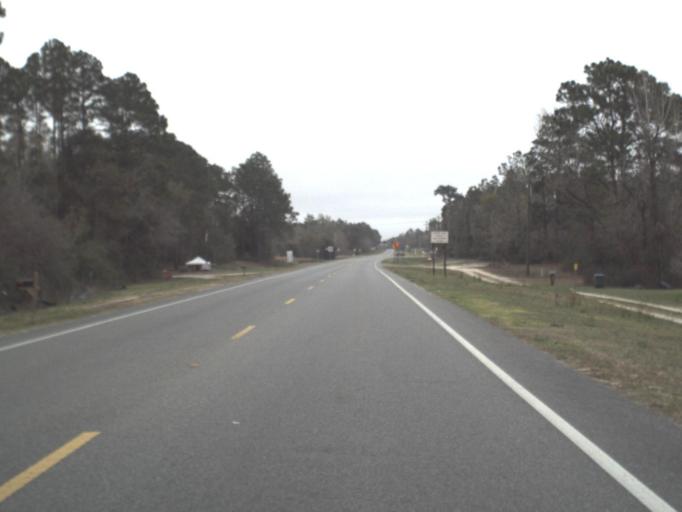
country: US
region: Florida
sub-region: Wakulla County
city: Crawfordville
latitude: 30.1399
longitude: -84.3179
